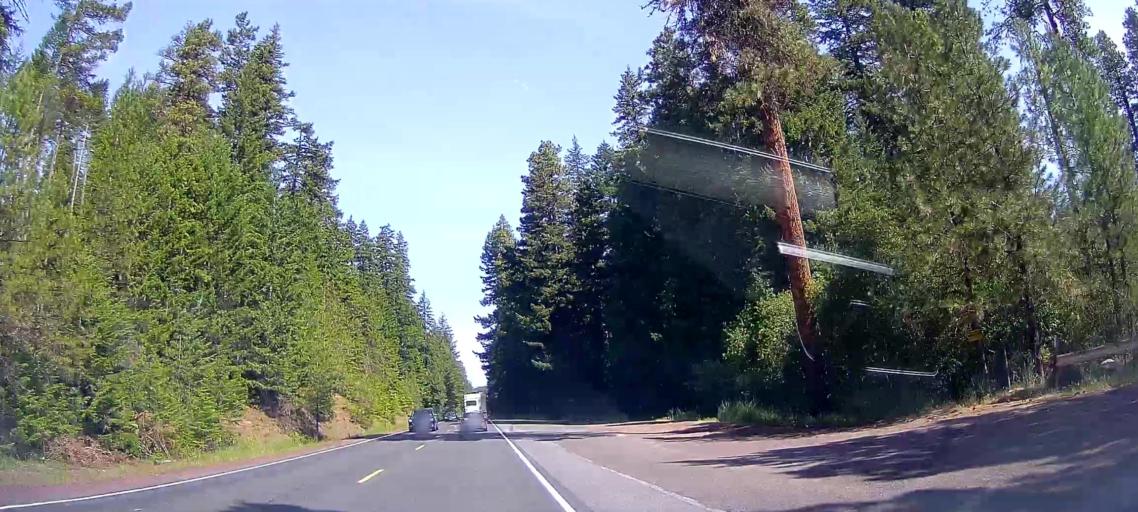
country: US
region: Oregon
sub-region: Jefferson County
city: Warm Springs
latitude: 45.0586
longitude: -121.5158
